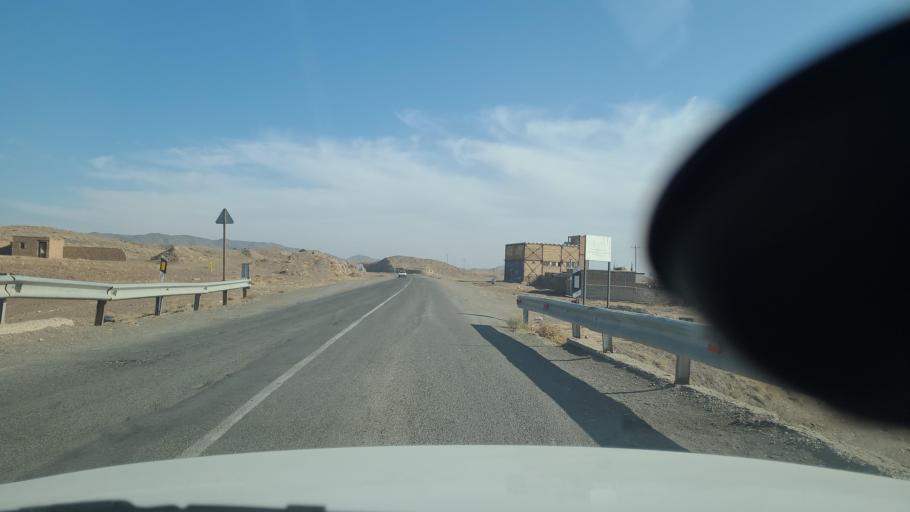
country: IR
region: Razavi Khorasan
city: Fariman
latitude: 35.5929
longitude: 59.6859
